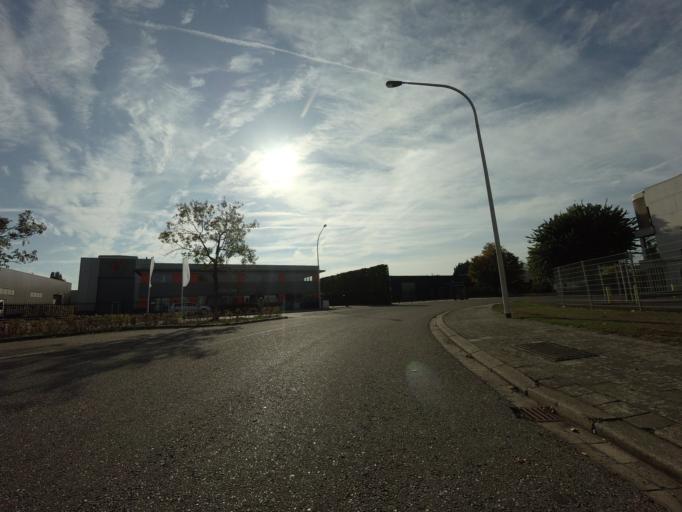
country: BE
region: Flanders
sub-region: Provincie Antwerpen
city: Wijnegem
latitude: 51.2316
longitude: 4.4989
